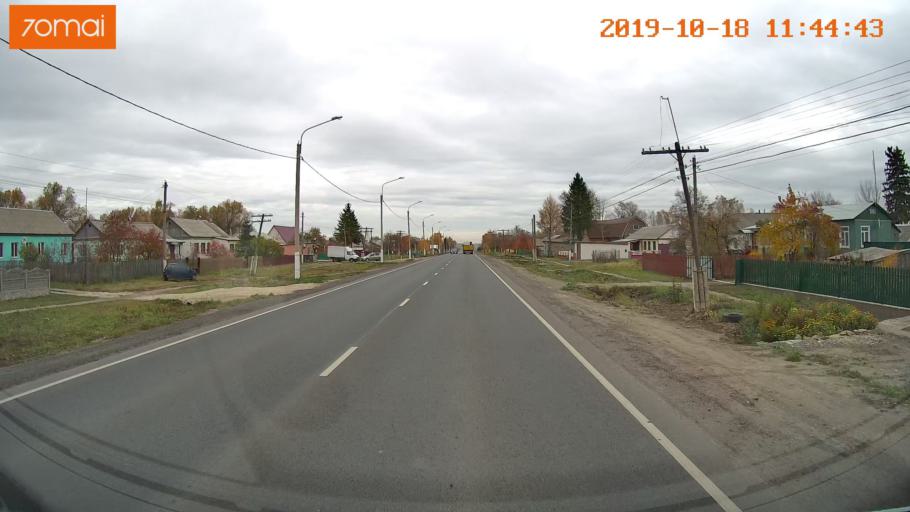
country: RU
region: Rjazan
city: Mikhaylov
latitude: 54.2045
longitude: 38.9613
